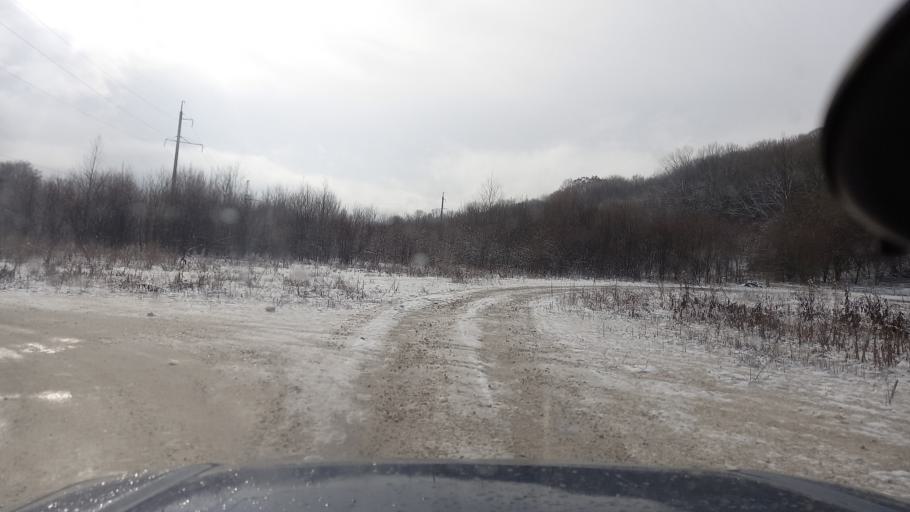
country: RU
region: Adygeya
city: Kamennomostskiy
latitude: 44.2453
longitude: 40.1978
